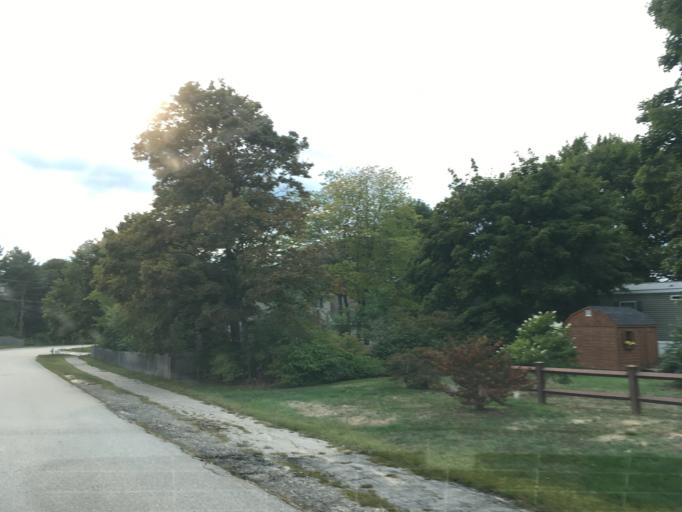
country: US
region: New Hampshire
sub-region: Rockingham County
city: Exeter
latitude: 42.9858
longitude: -70.9435
